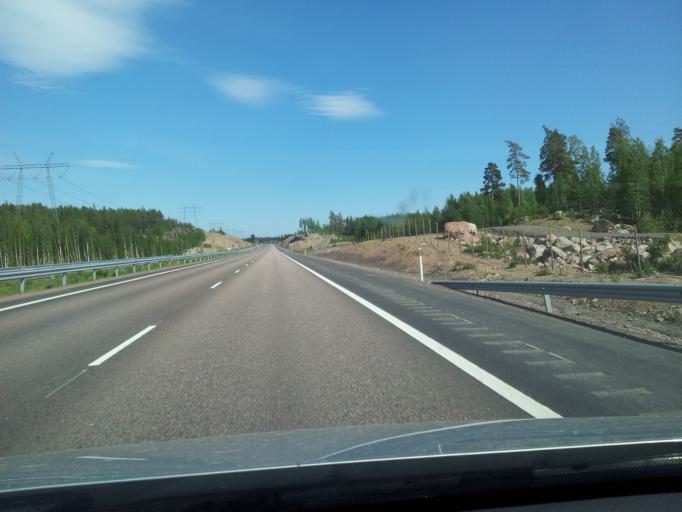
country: FI
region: Uusimaa
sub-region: Loviisa
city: Ruotsinpyhtaeae
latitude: 60.4890
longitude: 26.3482
